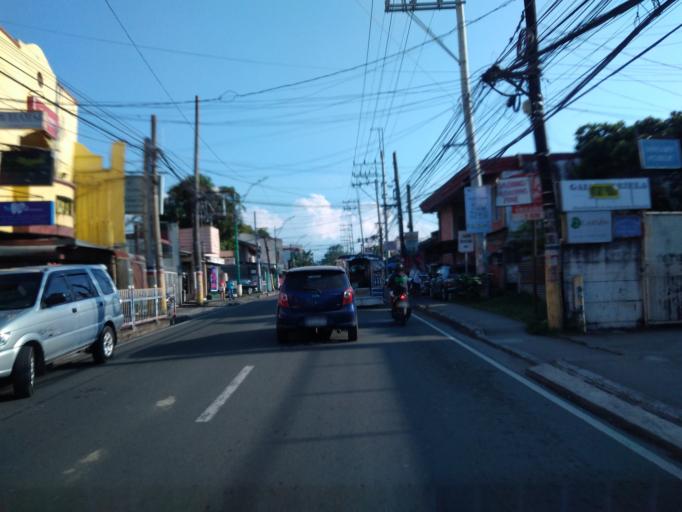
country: PH
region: Calabarzon
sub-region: Province of Laguna
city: Los Banos
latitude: 14.1768
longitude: 121.2427
